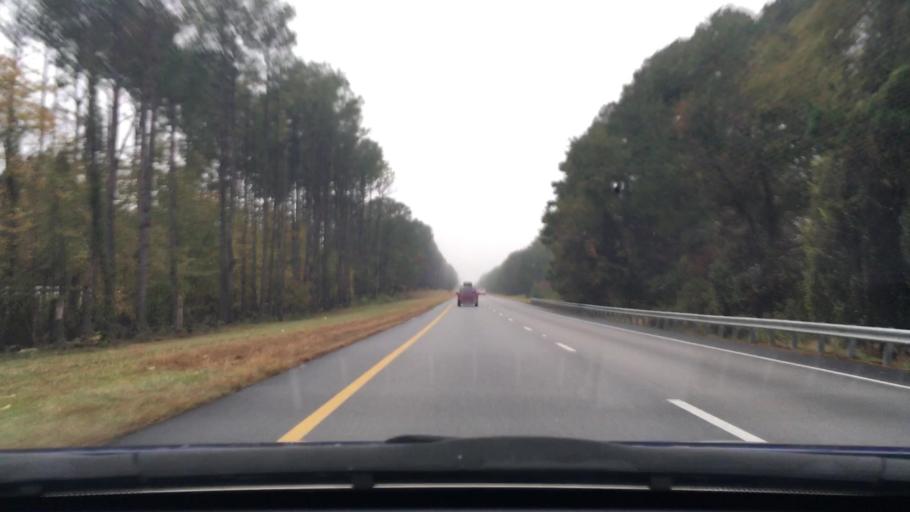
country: US
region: South Carolina
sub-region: Lee County
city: Bishopville
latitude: 34.2024
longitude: -80.3587
